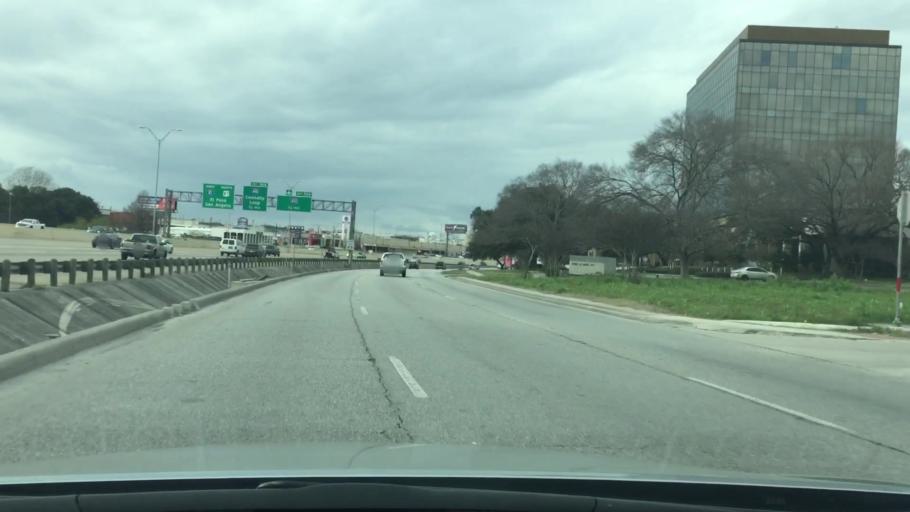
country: US
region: Texas
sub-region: Bexar County
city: Balcones Heights
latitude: 29.4859
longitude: -98.5408
